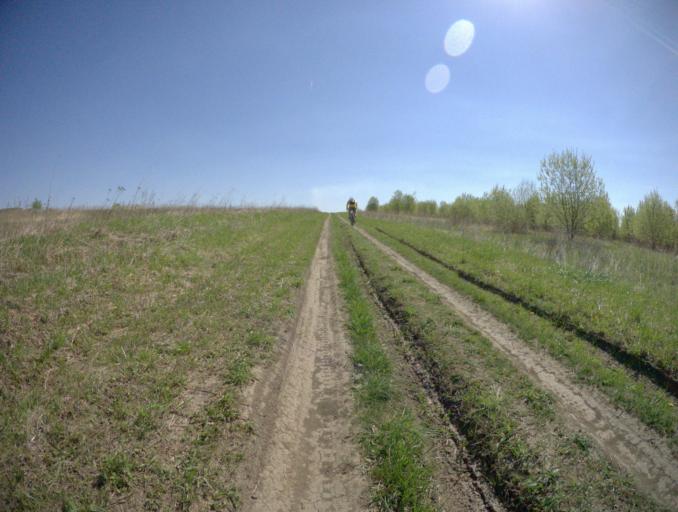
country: RU
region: Vladimir
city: Vladimir
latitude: 56.2903
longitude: 40.3548
